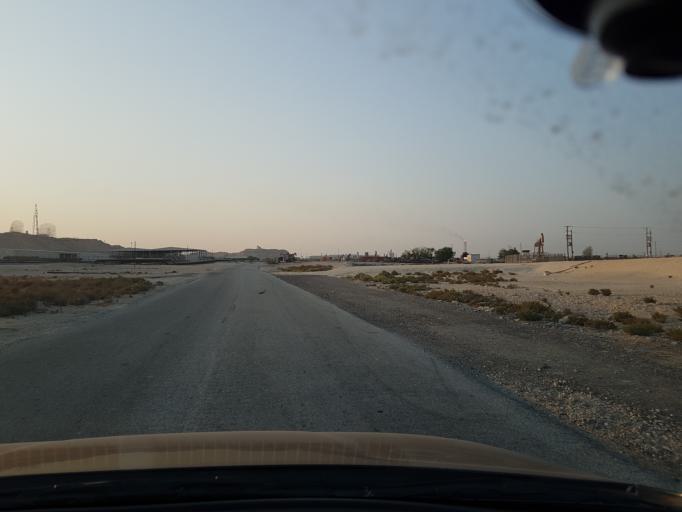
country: BH
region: Central Governorate
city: Dar Kulayb
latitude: 26.0217
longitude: 50.5571
